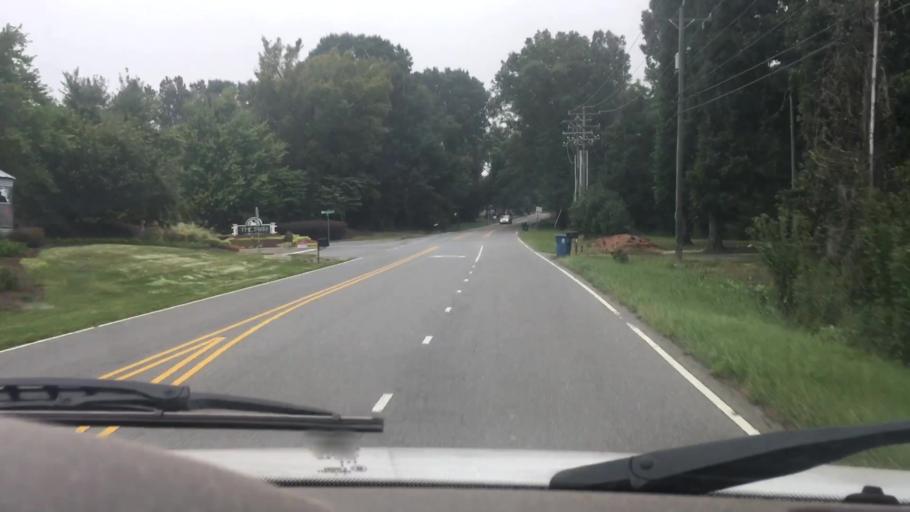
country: US
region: North Carolina
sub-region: Gaston County
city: Davidson
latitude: 35.4602
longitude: -80.7588
